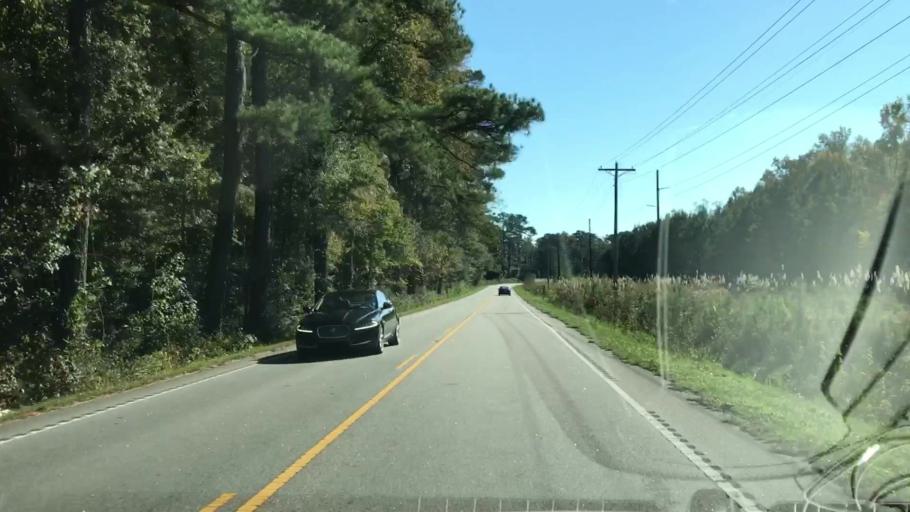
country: US
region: South Carolina
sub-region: Jasper County
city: Ridgeland
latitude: 32.5242
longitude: -80.8951
